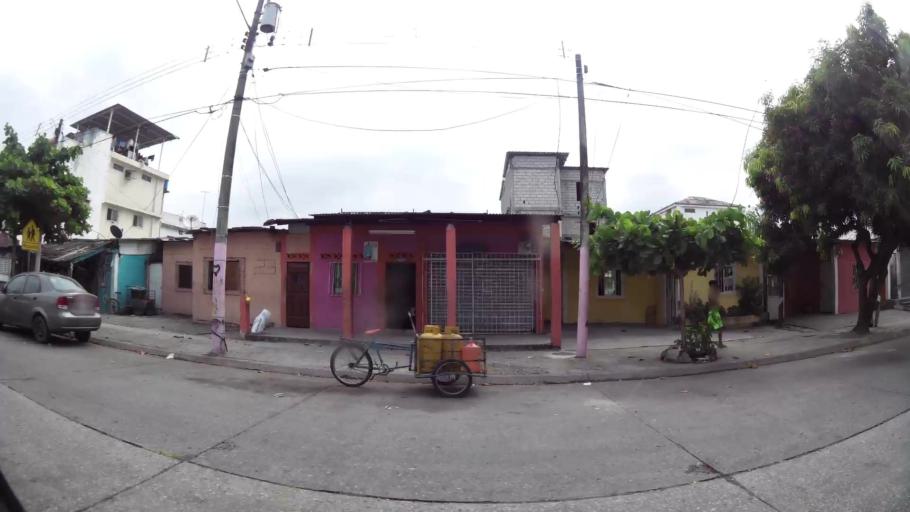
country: EC
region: Guayas
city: Eloy Alfaro
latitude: -2.1167
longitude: -79.8886
